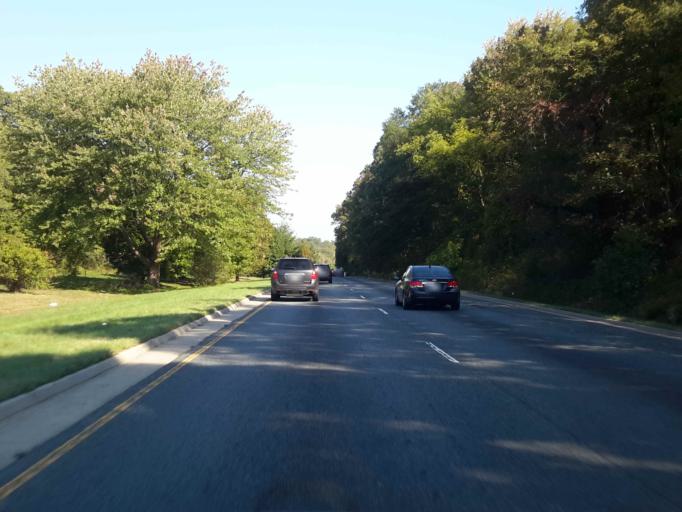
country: US
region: Maryland
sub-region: Prince George's County
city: Greenbelt
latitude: 39.0136
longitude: -76.8604
